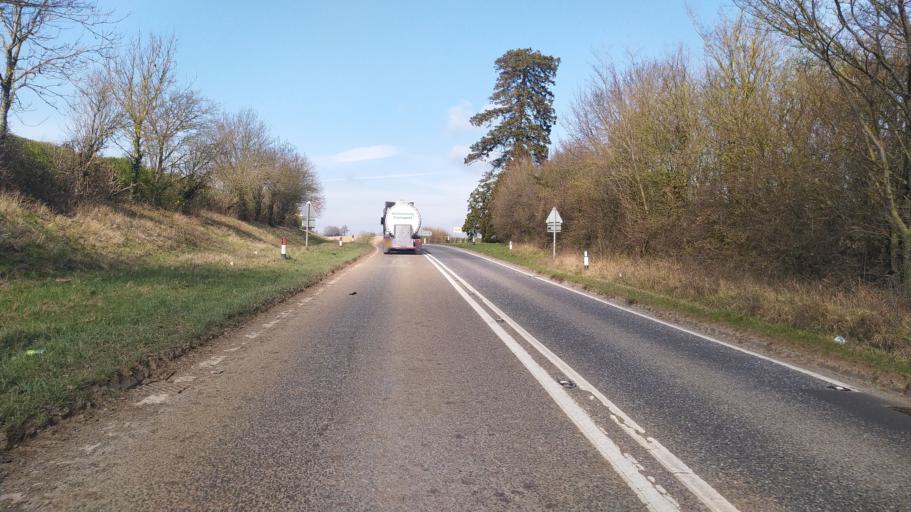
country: GB
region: England
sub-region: Somerset
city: Stoke-sub-Hamdon
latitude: 50.9472
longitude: -2.7701
